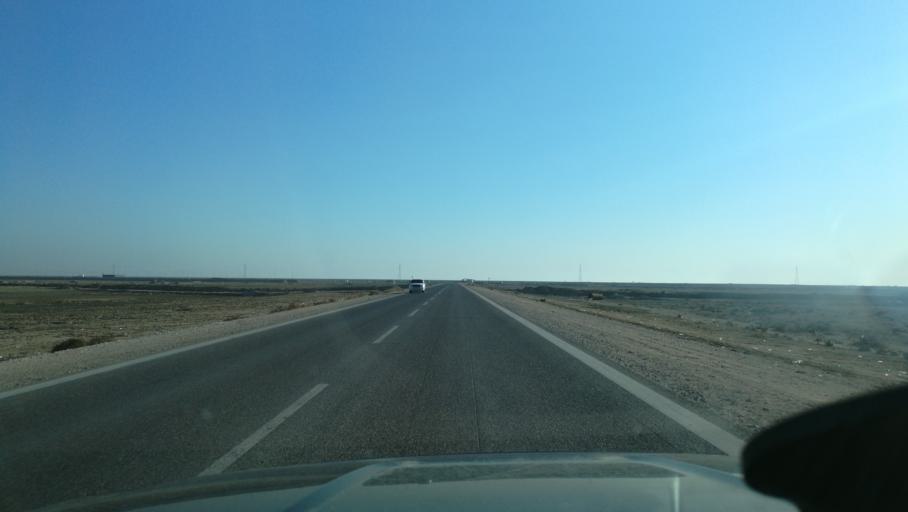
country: IQ
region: Dhi Qar
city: Suq ash Shuyukh
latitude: 30.8013
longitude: 46.3657
